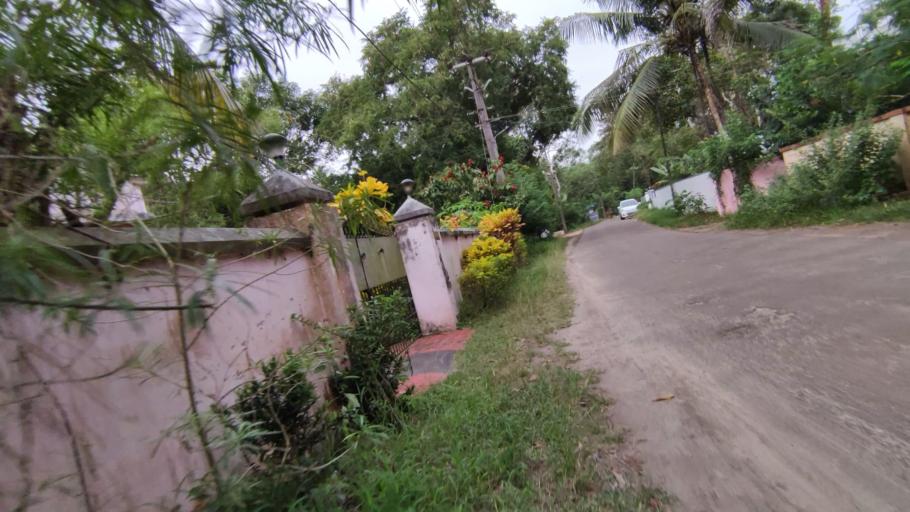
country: IN
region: Kerala
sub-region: Alappuzha
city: Shertallai
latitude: 9.6428
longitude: 76.3658
